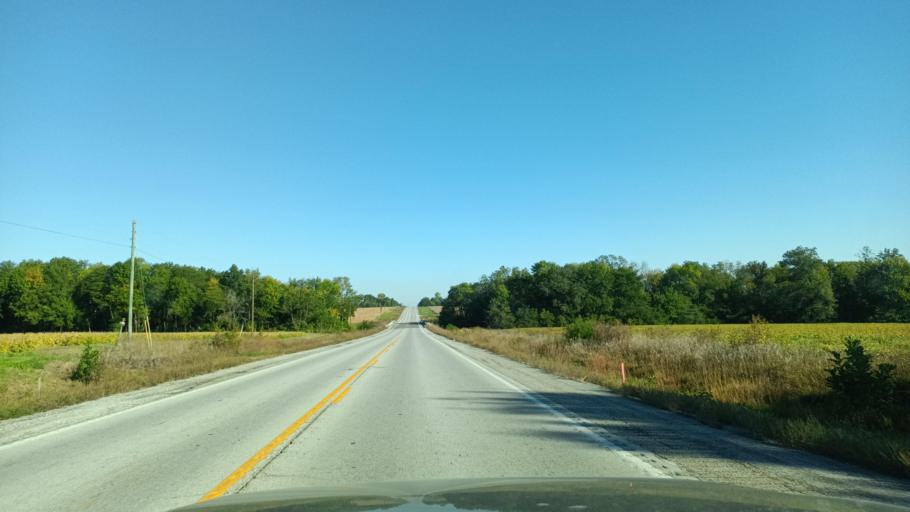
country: US
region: Missouri
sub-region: Audrain County
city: Vandalia
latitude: 39.3350
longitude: -91.6430
